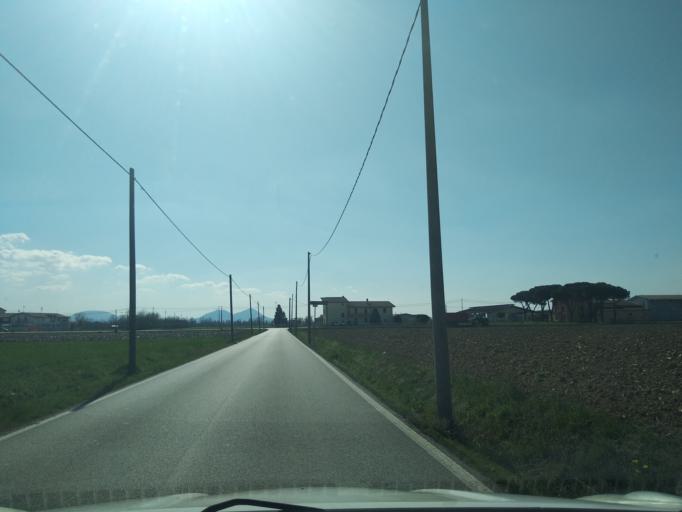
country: IT
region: Veneto
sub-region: Provincia di Padova
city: Villafranca Padovana
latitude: 45.4772
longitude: 11.7828
